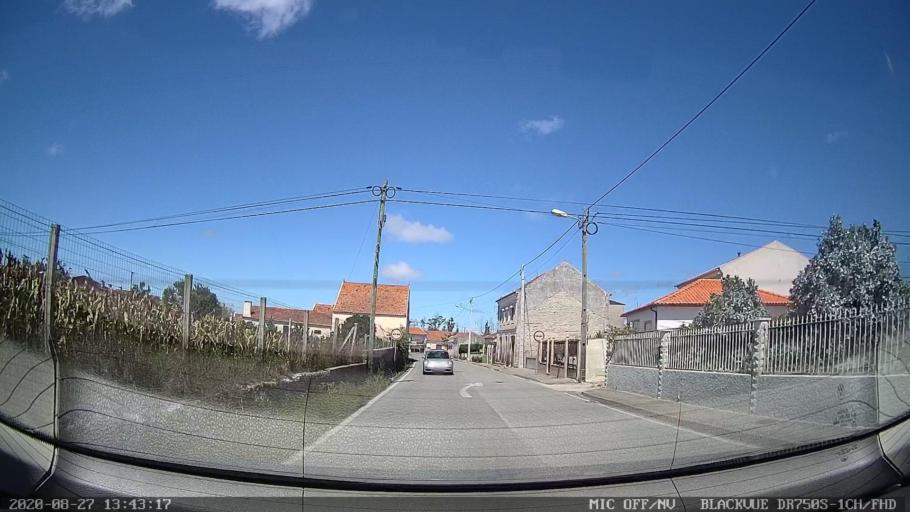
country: PT
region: Coimbra
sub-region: Mira
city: Mira
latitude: 40.4218
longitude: -8.7384
